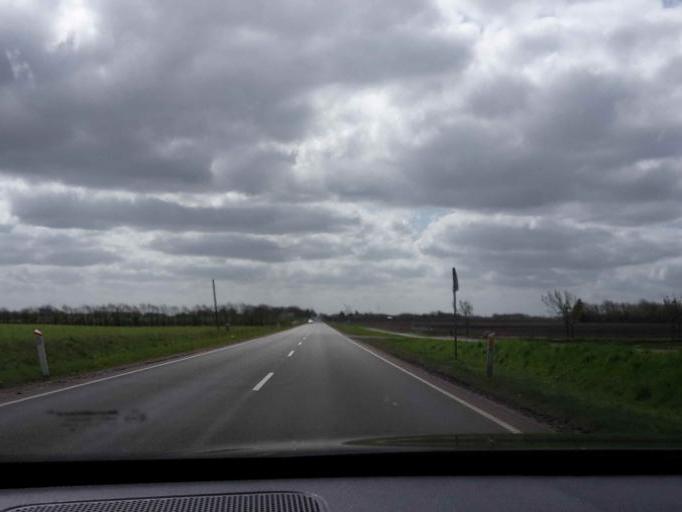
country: DK
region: South Denmark
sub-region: Varde Kommune
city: Olgod
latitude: 55.7588
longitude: 8.6200
